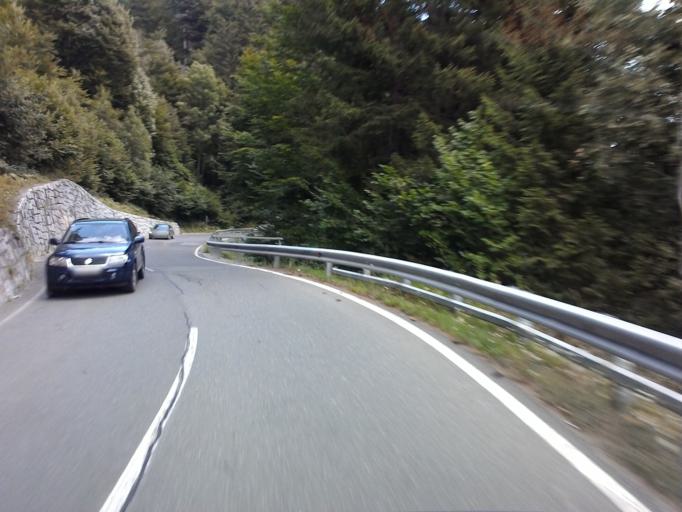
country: AT
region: Carinthia
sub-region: Politischer Bezirk Spittal an der Drau
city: Oberdrauburg
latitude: 46.6821
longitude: 12.9509
